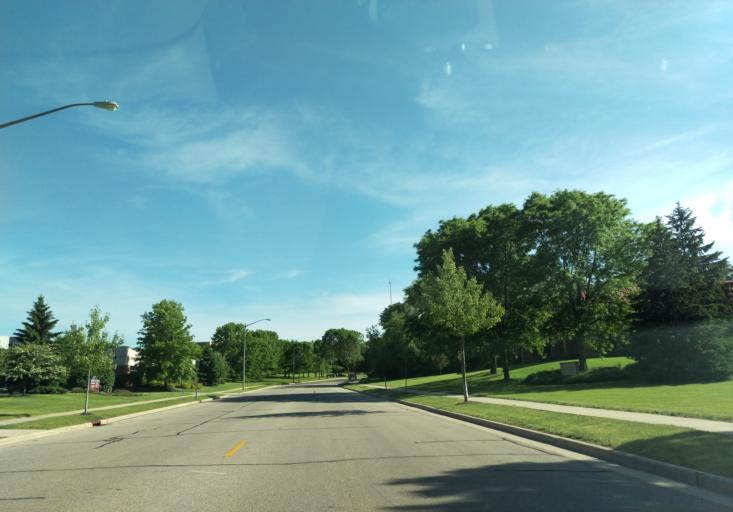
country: US
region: Wisconsin
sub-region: Dane County
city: Middleton
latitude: 43.0795
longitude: -89.5293
